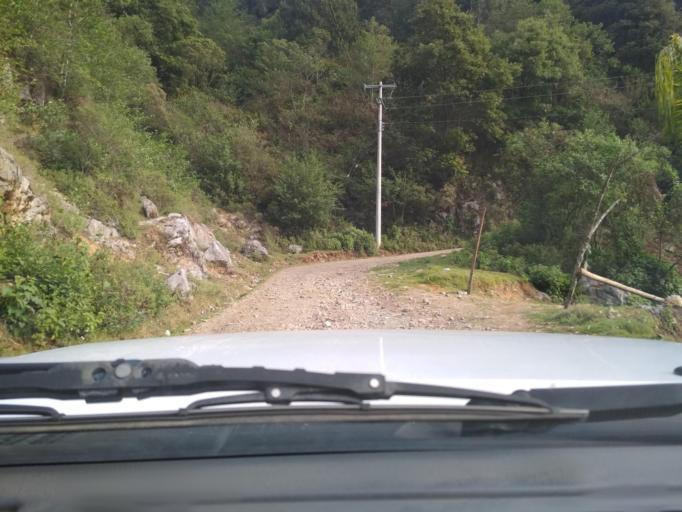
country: MX
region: Veracruz
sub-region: Soledad Atzompa
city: Tlatilpa
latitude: 18.7548
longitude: -97.1556
